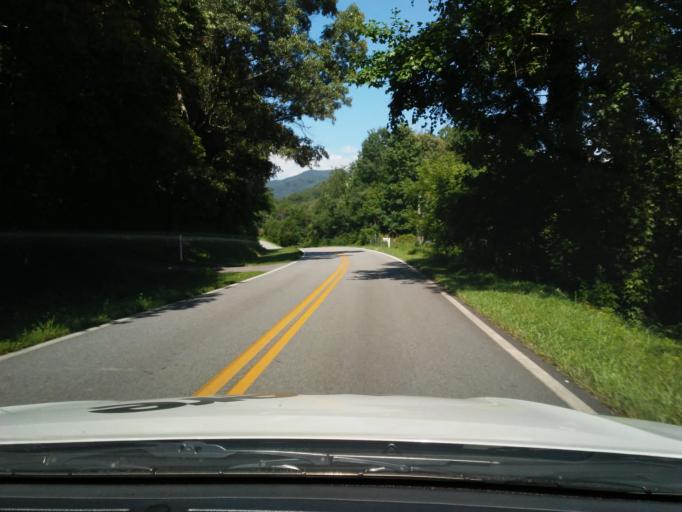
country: US
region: Georgia
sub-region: Union County
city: Blairsville
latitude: 34.9372
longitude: -83.8702
